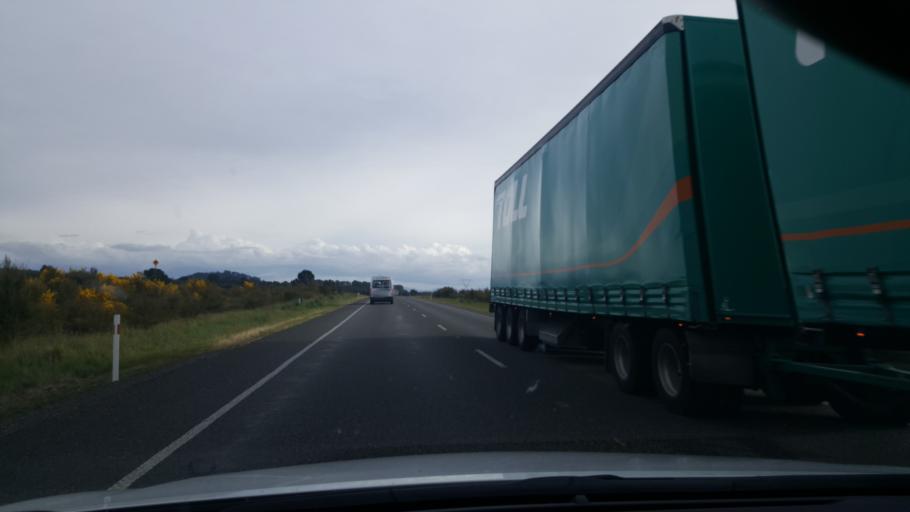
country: NZ
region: Waikato
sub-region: Taupo District
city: Taupo
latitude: -38.6896
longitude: 176.1139
